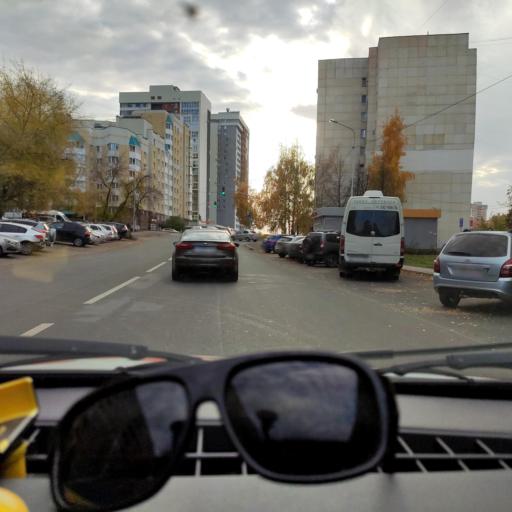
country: RU
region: Bashkortostan
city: Ufa
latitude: 54.7192
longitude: 55.9967
